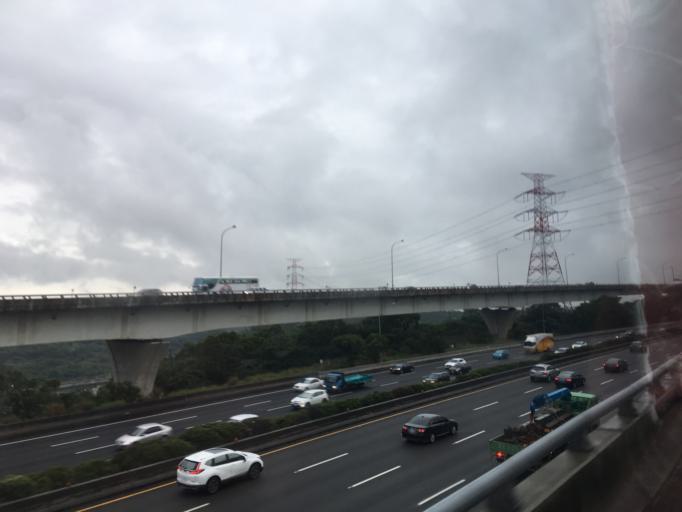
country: TW
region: Taiwan
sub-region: Taoyuan
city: Taoyuan
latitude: 25.0643
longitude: 121.3407
